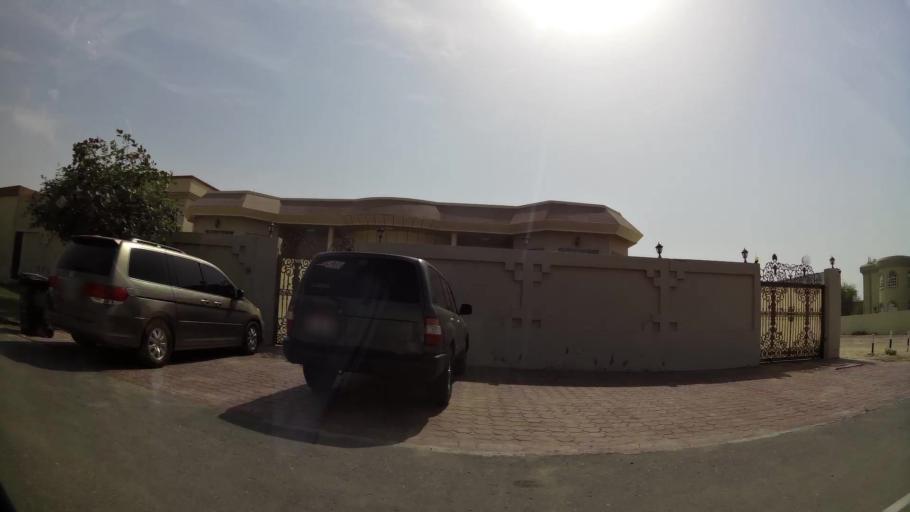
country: AE
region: Ash Shariqah
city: Sharjah
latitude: 25.2528
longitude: 55.4311
